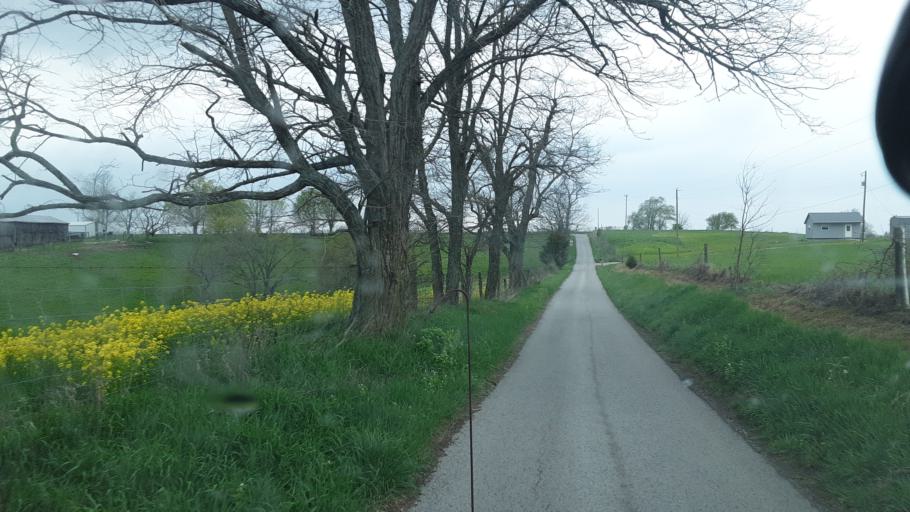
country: US
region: Kentucky
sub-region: Owen County
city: Owenton
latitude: 38.6094
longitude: -84.7694
